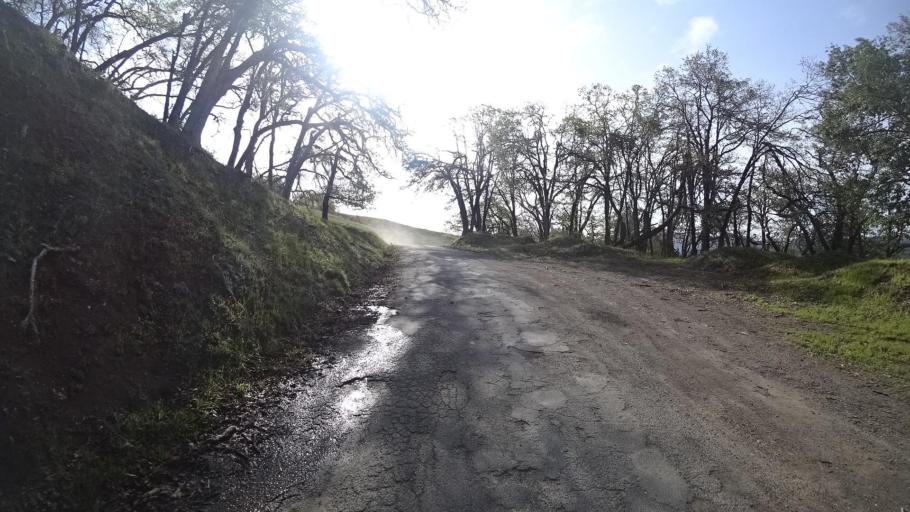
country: US
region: California
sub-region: Humboldt County
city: Hydesville
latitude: 40.6414
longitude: -123.8915
